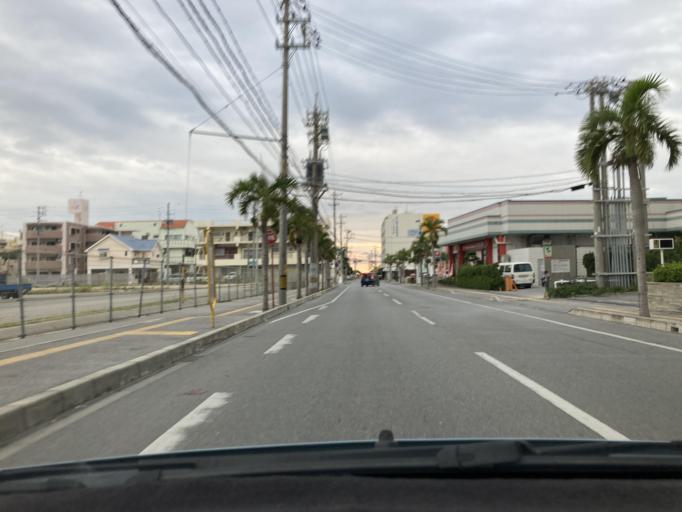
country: JP
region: Okinawa
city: Chatan
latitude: 26.3238
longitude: 127.7521
